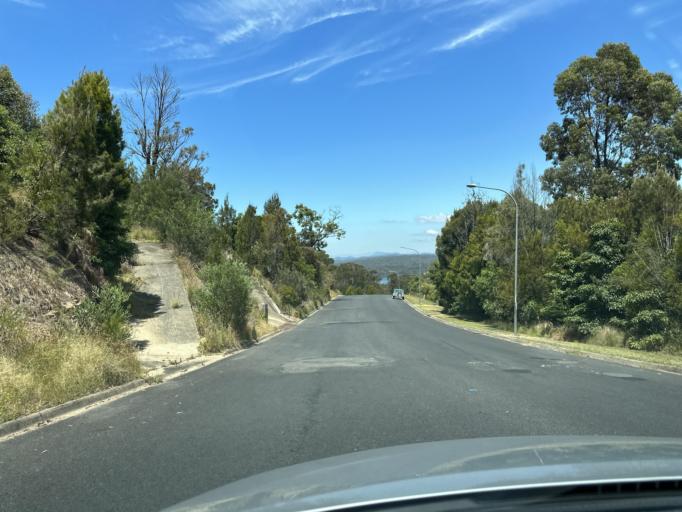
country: AU
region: New South Wales
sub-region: Bega Valley
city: Merimbula
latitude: -36.8901
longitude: 149.8967
